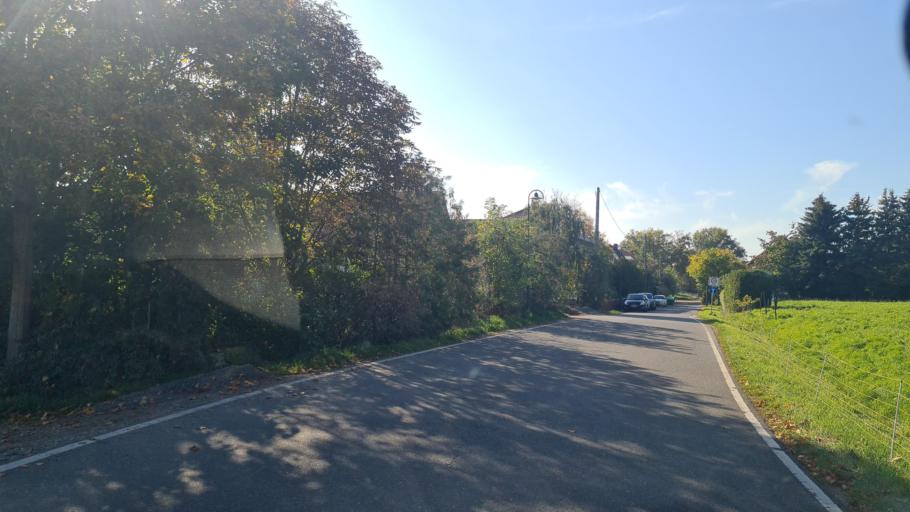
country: DE
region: Saxony
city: Borna
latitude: 51.1524
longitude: 12.4927
